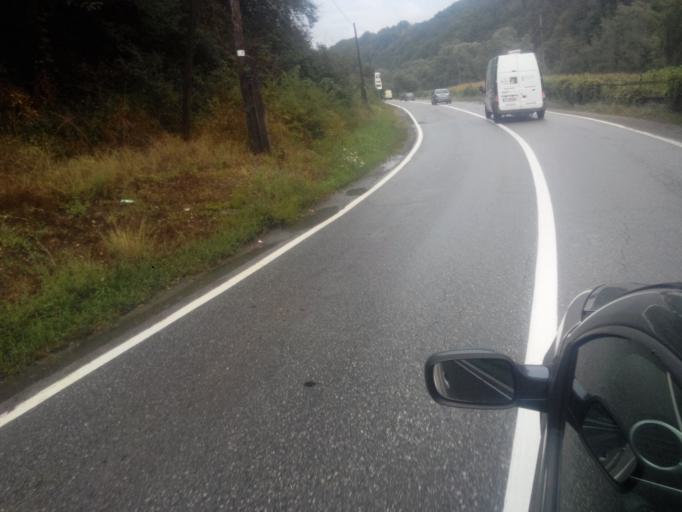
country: RO
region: Alba
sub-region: Comuna Ocolis
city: Ocolis
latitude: 46.4690
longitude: 23.4830
